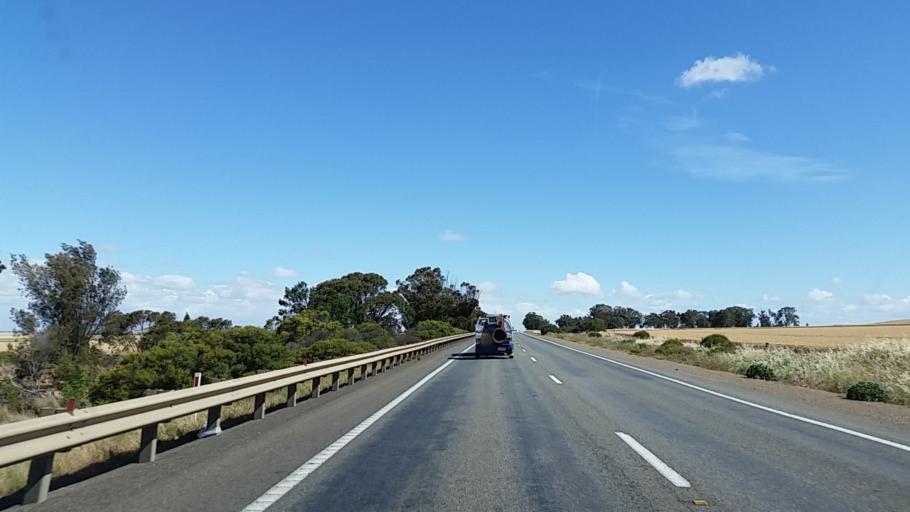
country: AU
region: South Australia
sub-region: Port Pirie City and Dists
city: Crystal Brook
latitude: -33.7026
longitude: 138.2118
